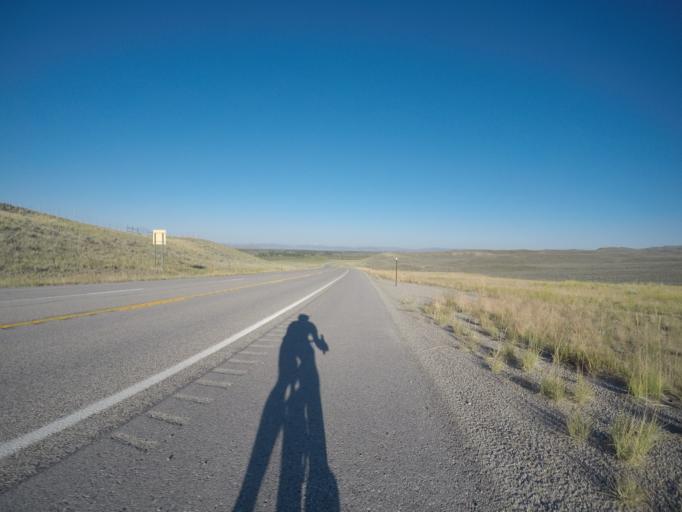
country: US
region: Wyoming
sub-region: Sublette County
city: Pinedale
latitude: 42.8821
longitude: -109.9844
